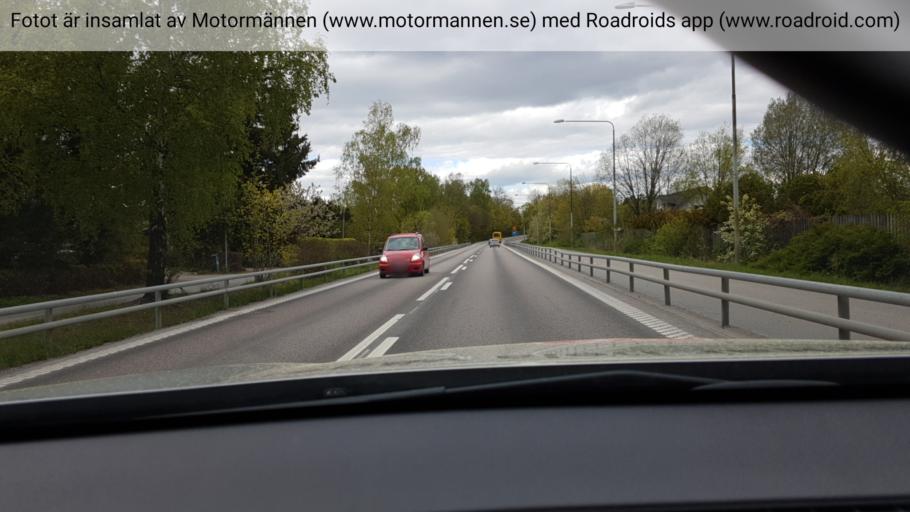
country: SE
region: Stockholm
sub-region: Tyreso Kommun
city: Bollmora
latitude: 59.2156
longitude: 18.2059
